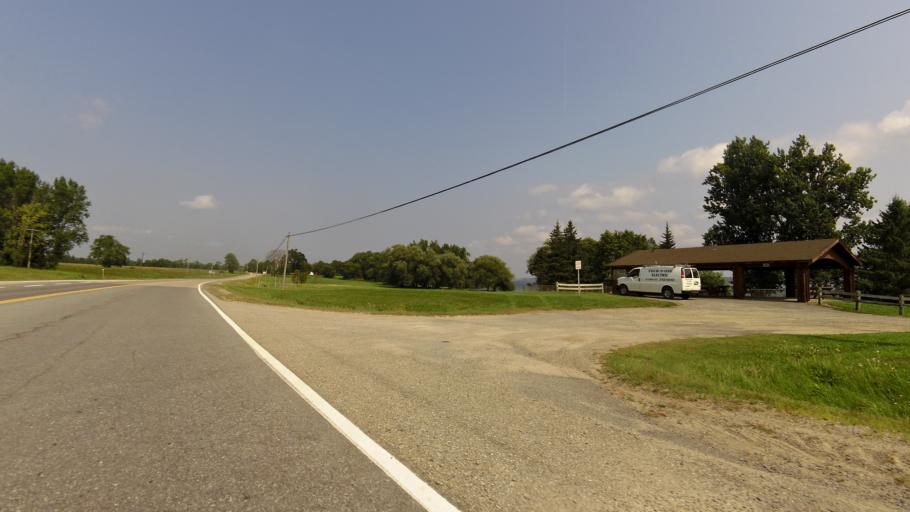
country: CA
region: Ontario
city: Prescott
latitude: 44.6667
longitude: -75.5716
